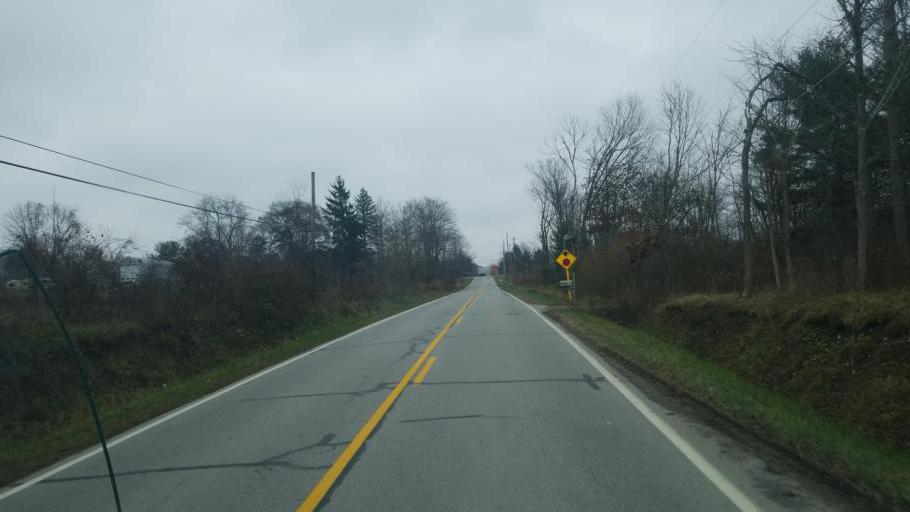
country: US
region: Ohio
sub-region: Medina County
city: Medina
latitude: 41.1359
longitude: -81.9270
